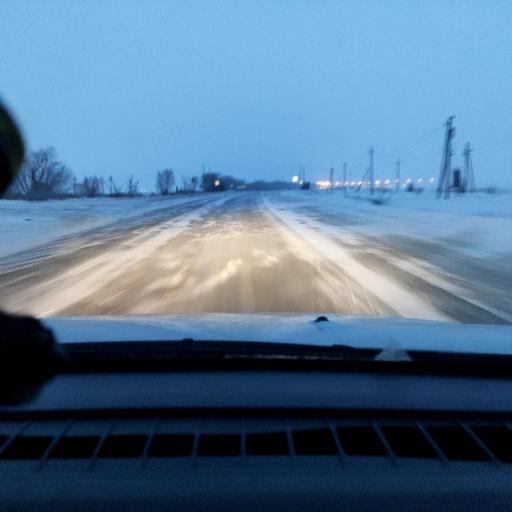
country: RU
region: Samara
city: Kinel'-Cherkassy
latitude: 53.4477
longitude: 51.5333
